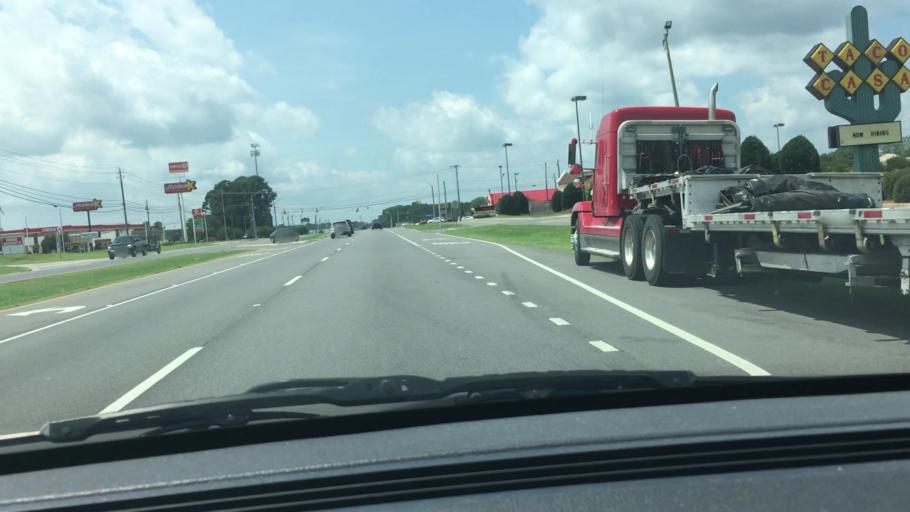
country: US
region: Alabama
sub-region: Tuscaloosa County
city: Northport
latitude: 33.2365
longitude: -87.6079
